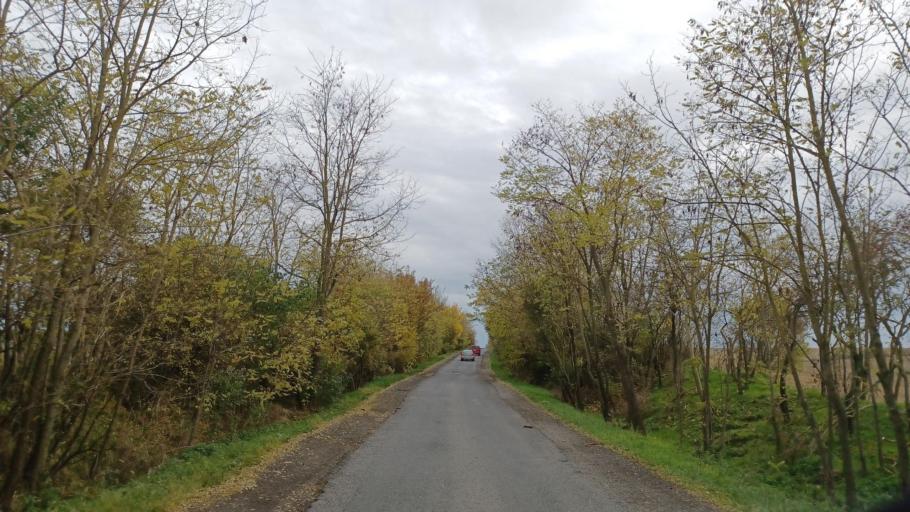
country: HU
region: Tolna
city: Nagydorog
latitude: 46.6830
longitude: 18.5985
